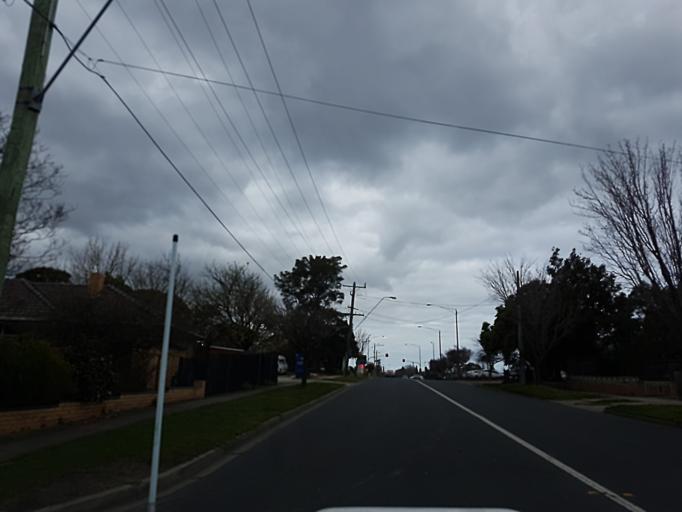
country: AU
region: Victoria
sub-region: Whitehorse
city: Blackburn North
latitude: -37.8076
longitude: 145.1409
